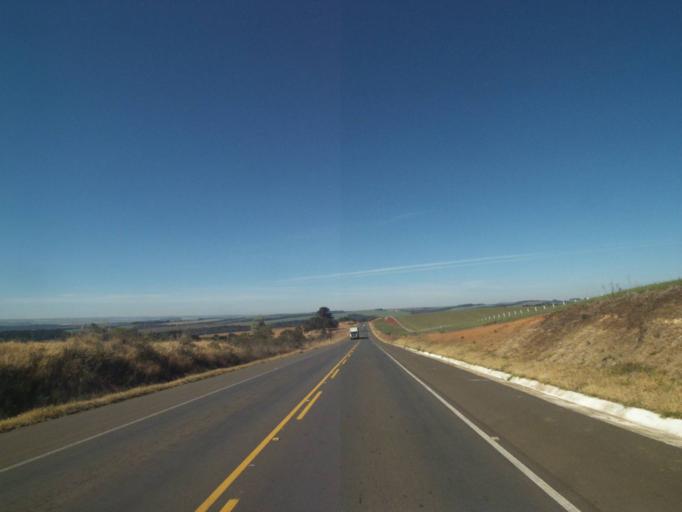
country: BR
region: Parana
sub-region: Tibagi
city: Tibagi
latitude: -24.6411
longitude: -50.4573
